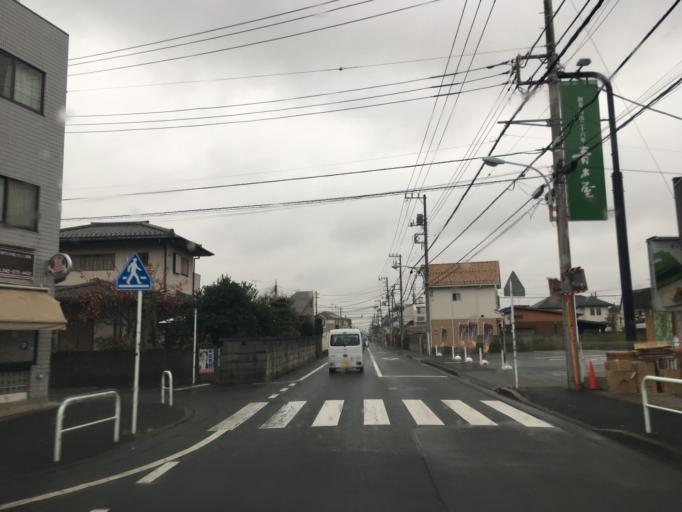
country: JP
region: Tokyo
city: Kokubunji
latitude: 35.7137
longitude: 139.4321
